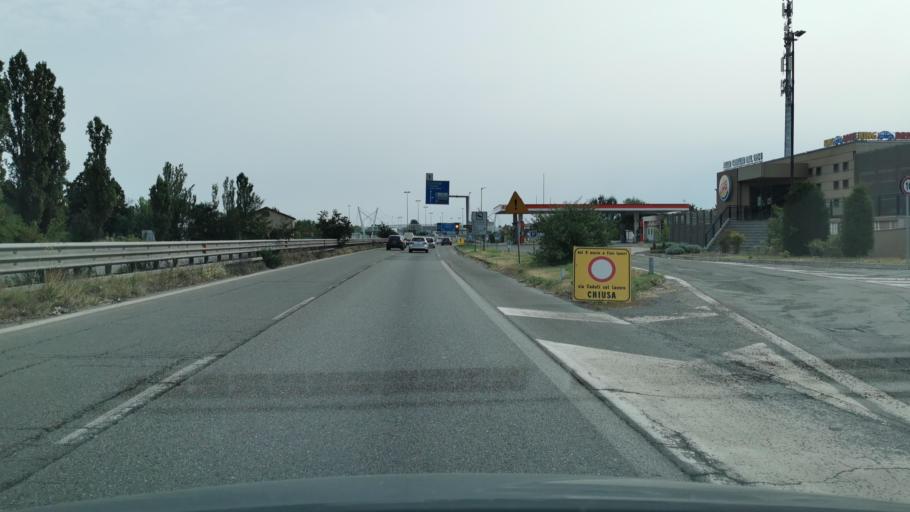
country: IT
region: Emilia-Romagna
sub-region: Provincia di Modena
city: Modena
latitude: 44.6300
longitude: 10.9540
